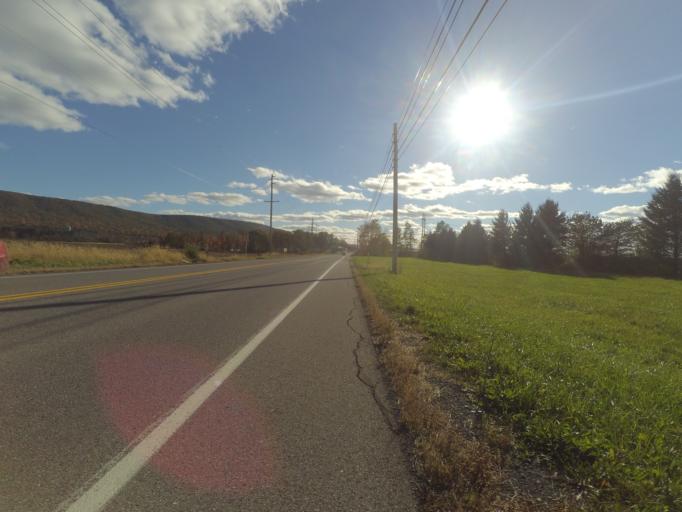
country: US
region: Pennsylvania
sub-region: Centre County
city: Houserville
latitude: 40.8483
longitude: -77.7925
